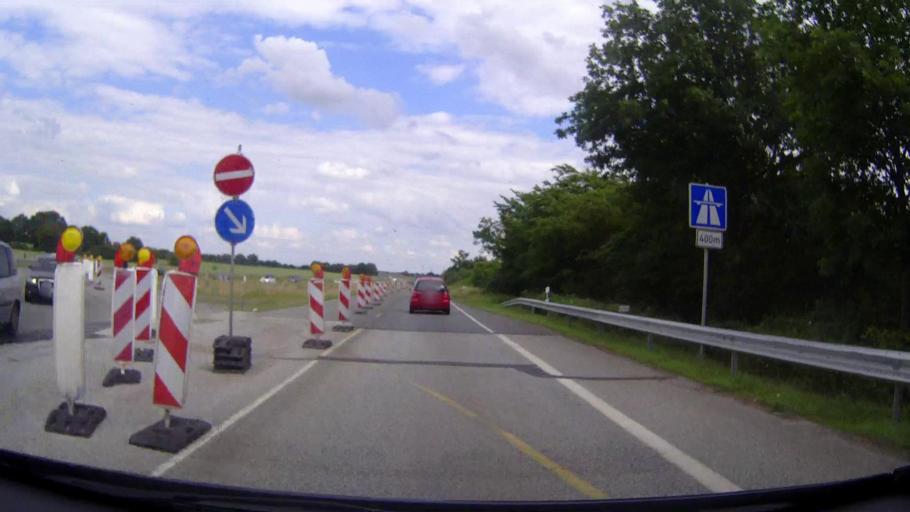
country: DE
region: Schleswig-Holstein
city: Klein Gladebrugge
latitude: 53.9217
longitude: 10.3387
